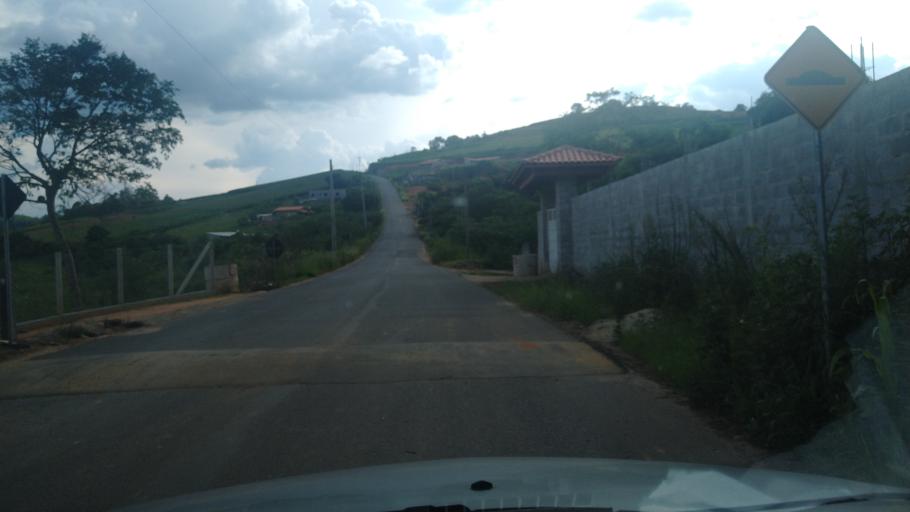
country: BR
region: Minas Gerais
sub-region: Extrema
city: Extrema
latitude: -22.7324
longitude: -46.3632
